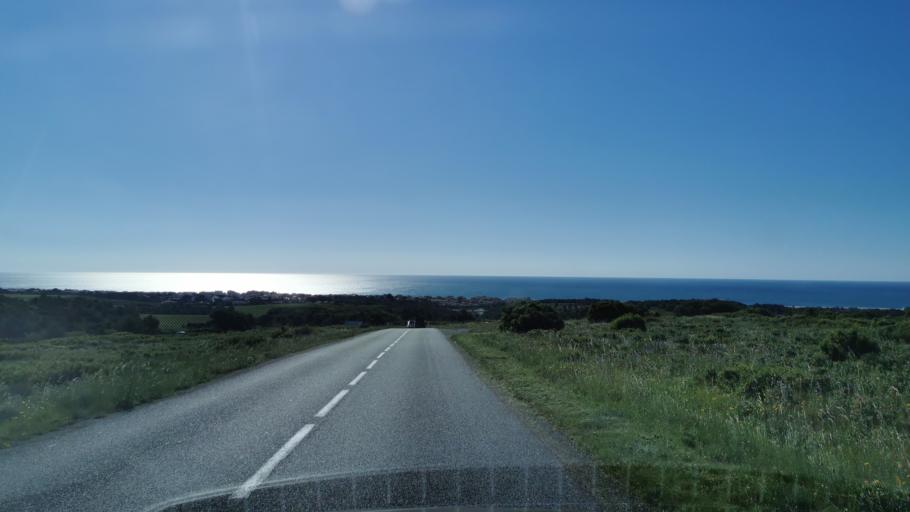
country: FR
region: Languedoc-Roussillon
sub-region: Departement de l'Aude
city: Armissan
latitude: 43.1608
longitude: 3.1395
